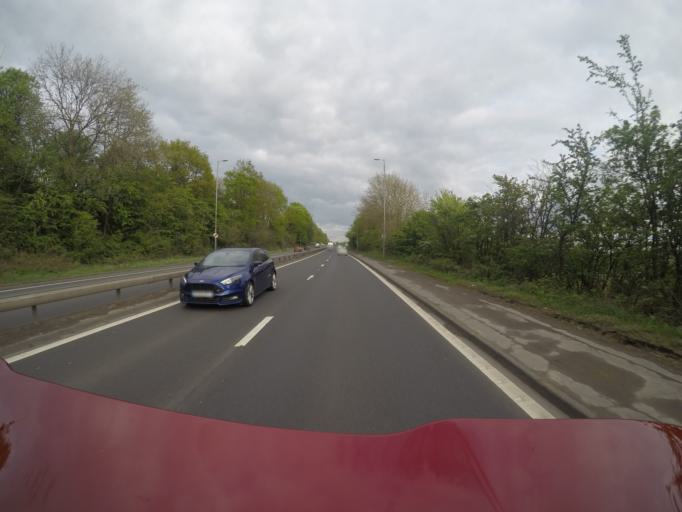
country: GB
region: Scotland
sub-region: West Dunbartonshire
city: Old Kilpatrick
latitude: 55.9278
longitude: -4.4601
